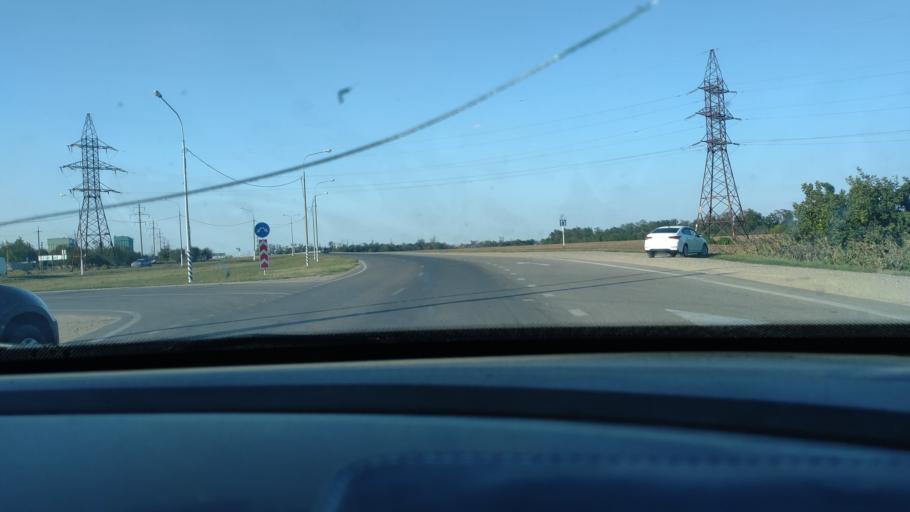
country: RU
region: Krasnodarskiy
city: Timashevsk
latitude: 45.6090
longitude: 38.9868
